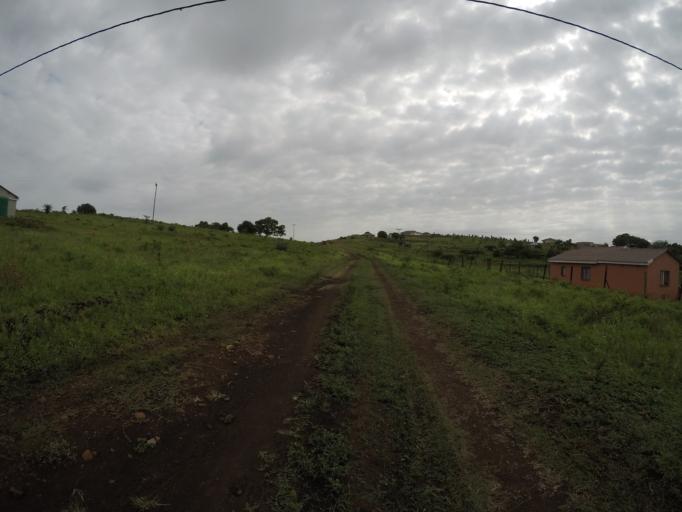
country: ZA
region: KwaZulu-Natal
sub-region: uThungulu District Municipality
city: Empangeni
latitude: -28.6383
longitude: 31.9040
